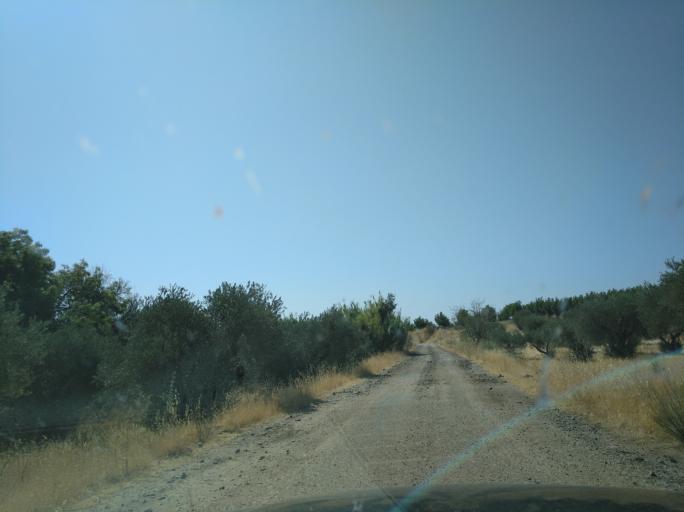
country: PT
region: Portalegre
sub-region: Campo Maior
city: Campo Maior
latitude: 39.0656
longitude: -7.0126
